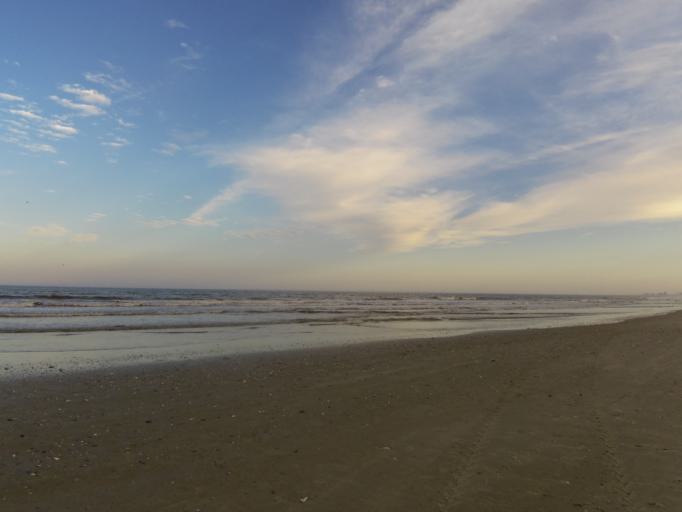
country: US
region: Florida
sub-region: Duval County
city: Atlantic Beach
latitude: 30.3760
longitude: -81.3971
